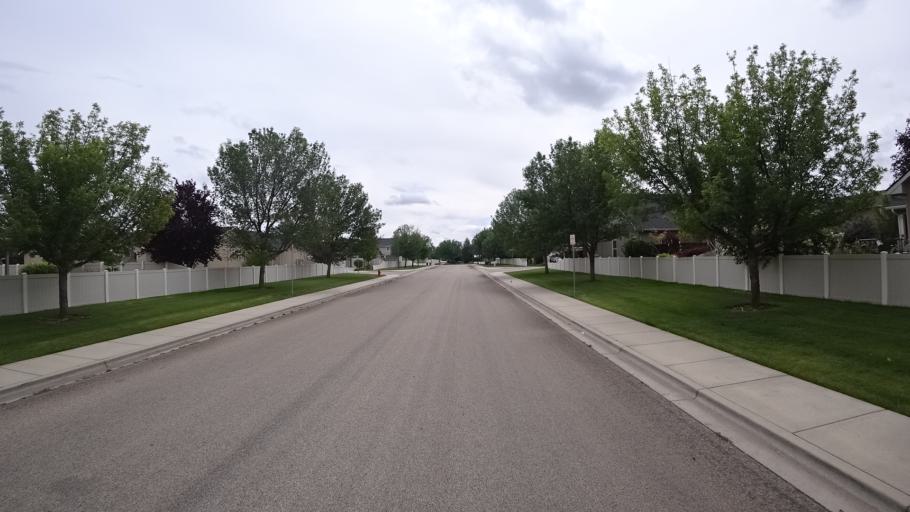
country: US
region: Idaho
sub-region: Ada County
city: Meridian
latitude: 43.6444
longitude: -116.4016
